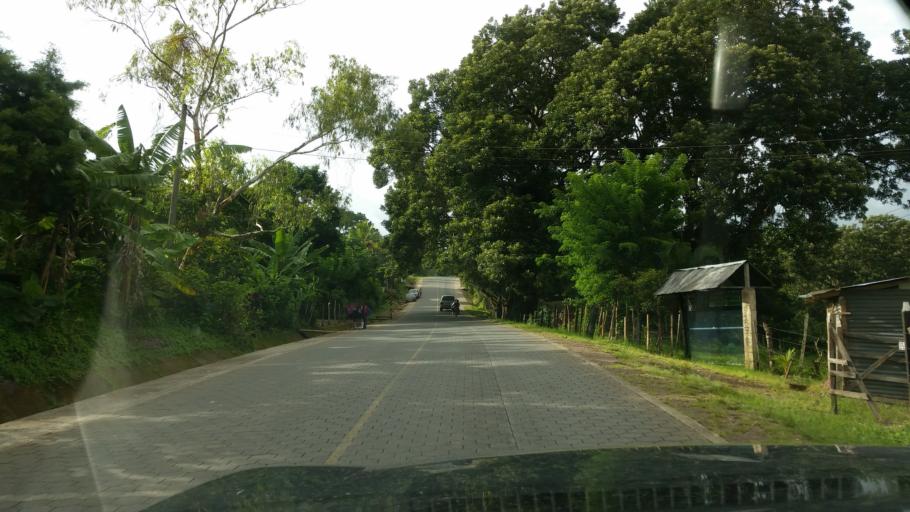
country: NI
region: Matagalpa
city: San Ramon
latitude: 13.1561
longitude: -85.7313
